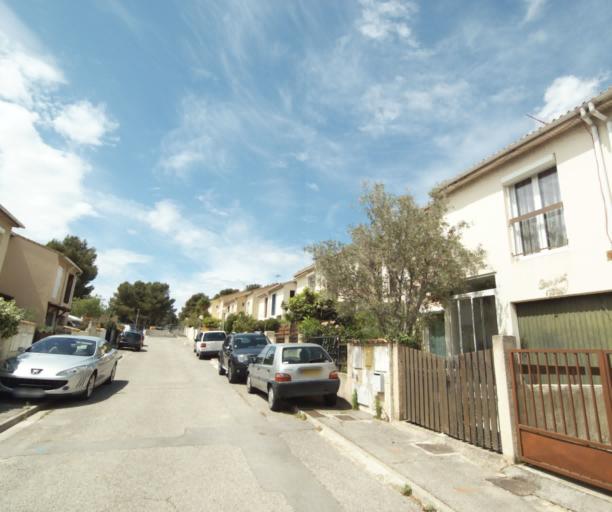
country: FR
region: Provence-Alpes-Cote d'Azur
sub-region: Departement des Bouches-du-Rhone
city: Rognac
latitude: 43.4967
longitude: 5.2347
